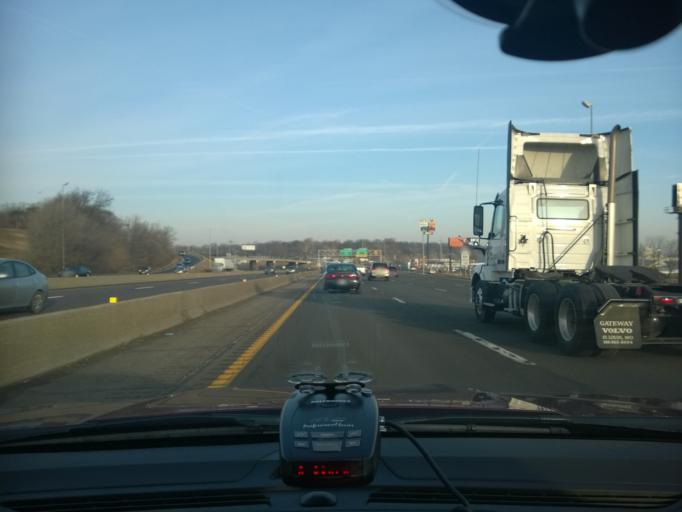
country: US
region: Illinois
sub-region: Madison County
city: Venice
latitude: 38.6821
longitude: -90.2150
